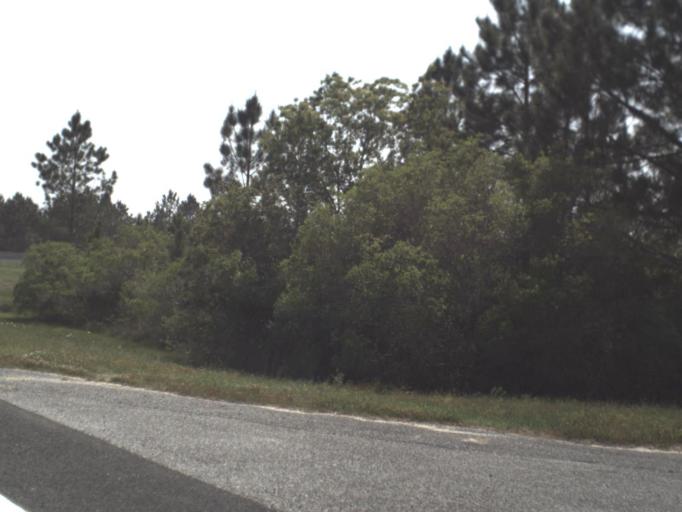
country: US
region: Florida
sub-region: Santa Rosa County
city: Tiger Point
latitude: 30.4847
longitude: -87.0797
